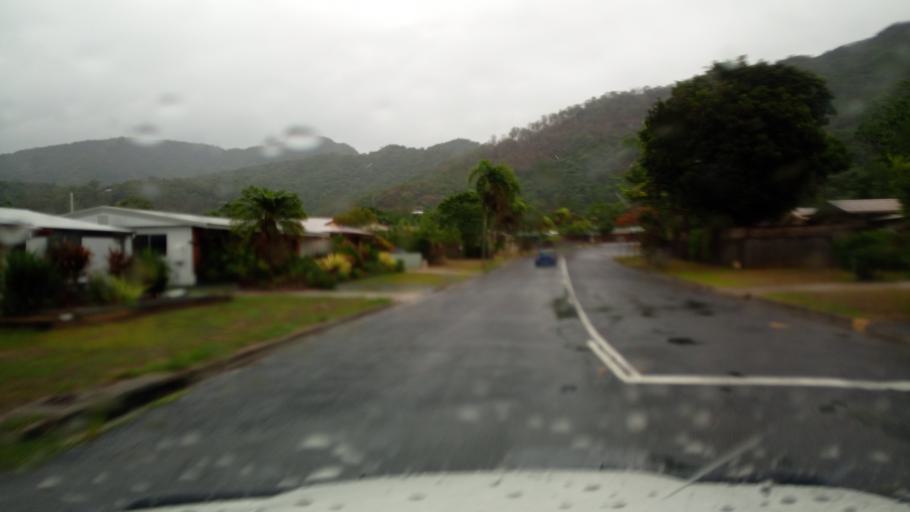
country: AU
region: Queensland
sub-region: Cairns
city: Woree
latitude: -16.9376
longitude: 145.7319
